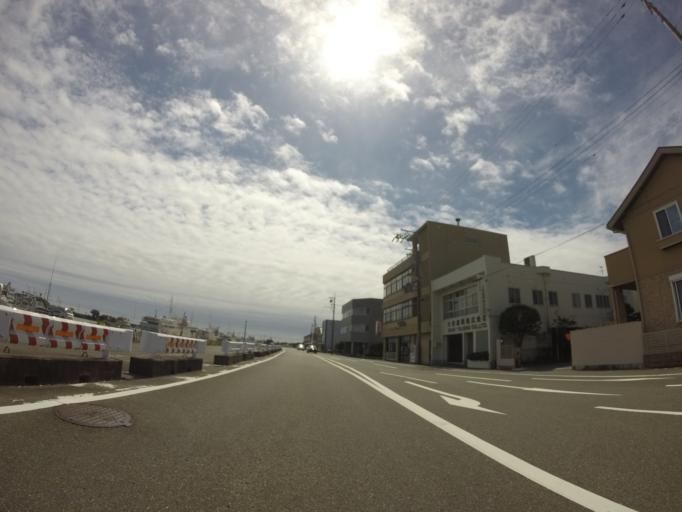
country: JP
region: Shizuoka
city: Yaizu
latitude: 34.8723
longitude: 138.3240
